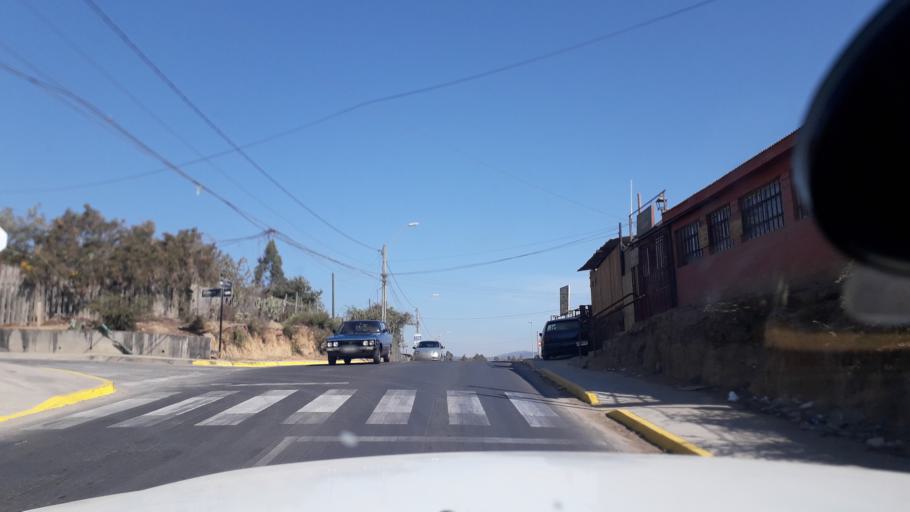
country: CL
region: Valparaiso
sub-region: Provincia de Marga Marga
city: Villa Alemana
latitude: -33.0643
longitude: -71.4029
